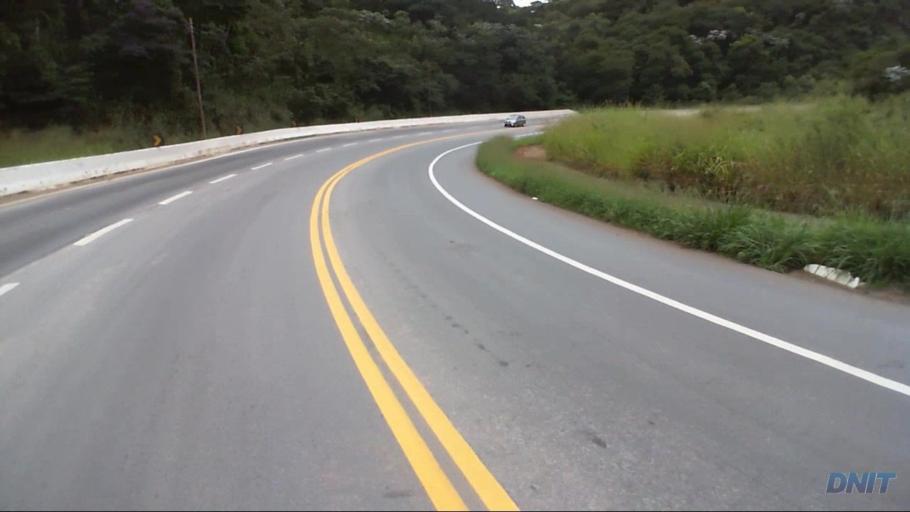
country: BR
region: Minas Gerais
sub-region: Caete
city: Caete
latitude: -19.7355
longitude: -43.5154
